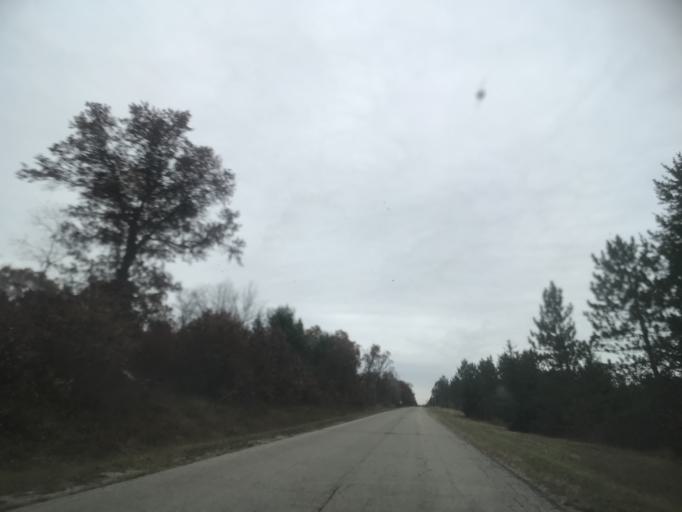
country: US
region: Wisconsin
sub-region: Oconto County
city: Gillett
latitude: 45.2930
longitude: -88.2568
